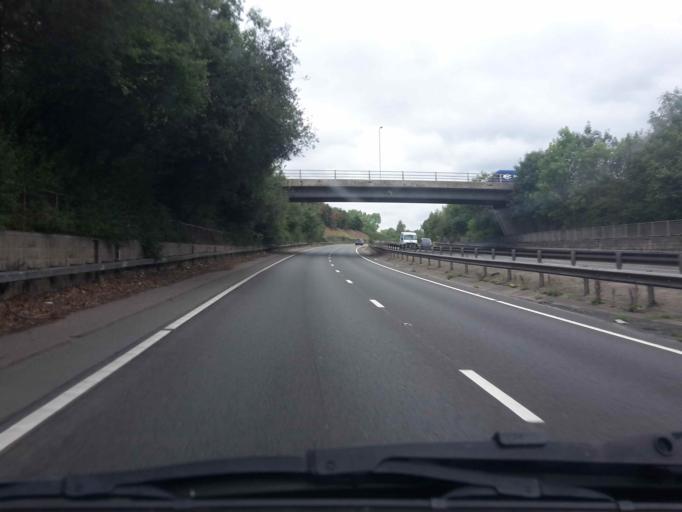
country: GB
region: England
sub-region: Hampshire
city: Aldershot
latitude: 51.2603
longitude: -0.7346
